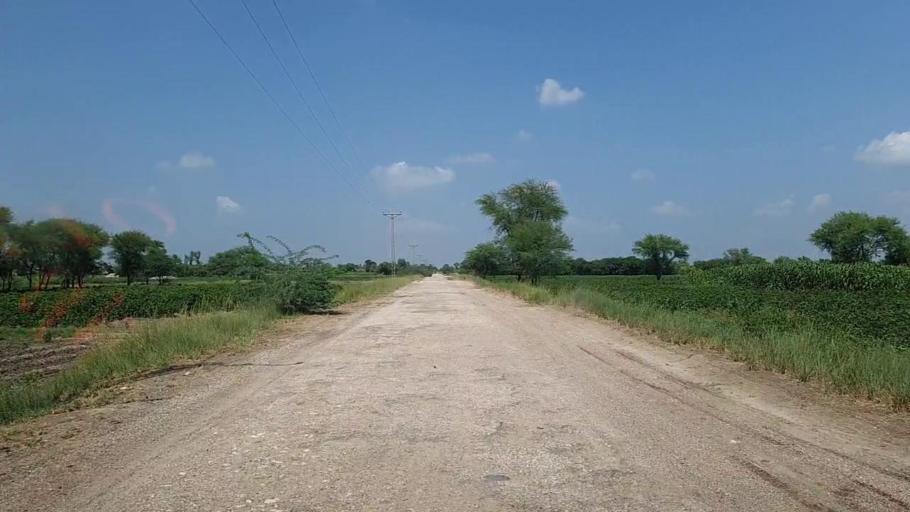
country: PK
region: Sindh
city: Kandiaro
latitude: 26.9942
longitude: 68.2510
